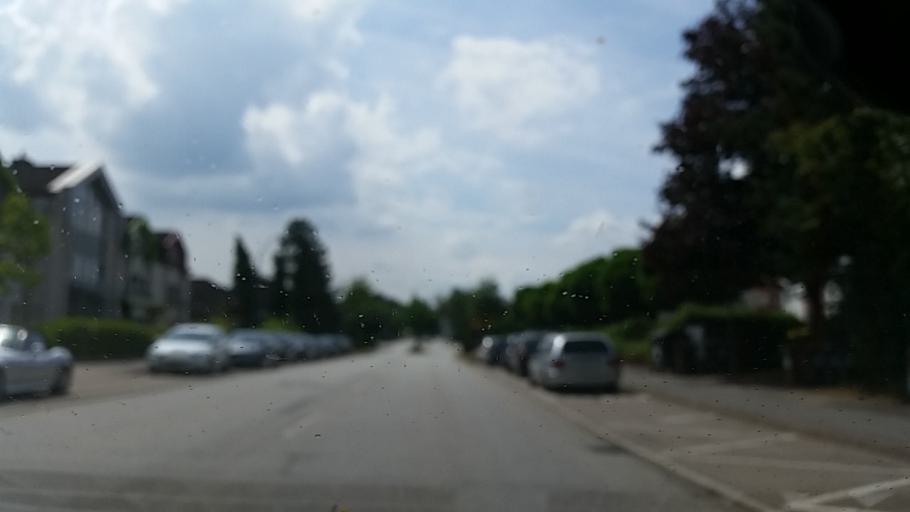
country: DE
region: Schleswig-Holstein
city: Bad Oldesloe
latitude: 53.8048
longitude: 10.3626
